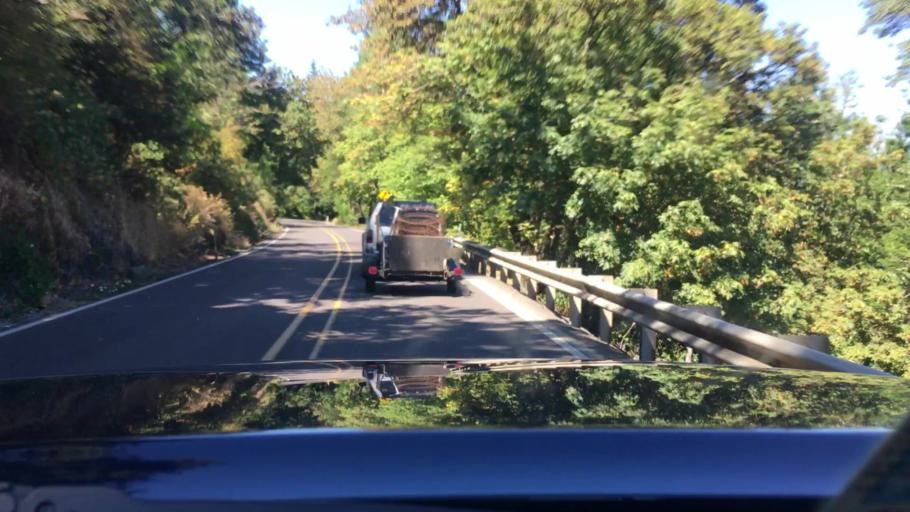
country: US
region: Oregon
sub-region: Lane County
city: Cottage Grove
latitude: 43.8234
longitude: -123.0457
